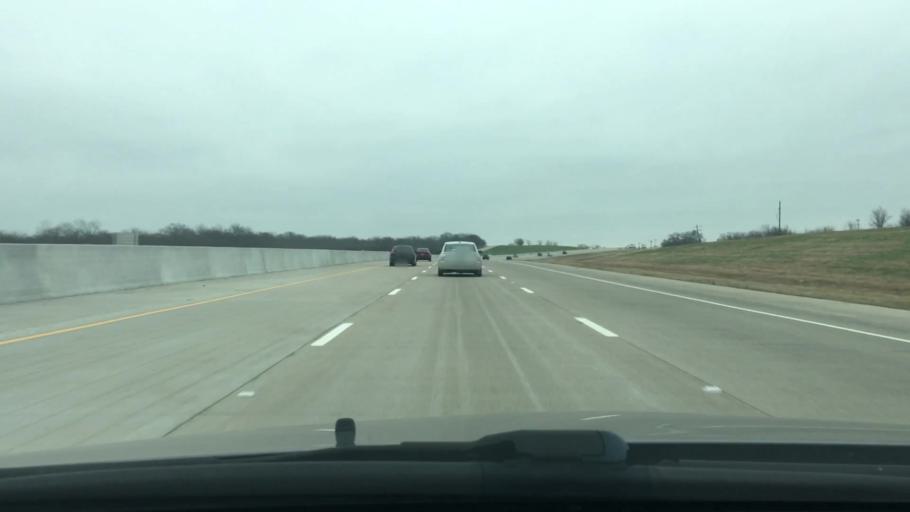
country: US
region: Texas
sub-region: Freestone County
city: Wortham
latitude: 31.8905
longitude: -96.3571
